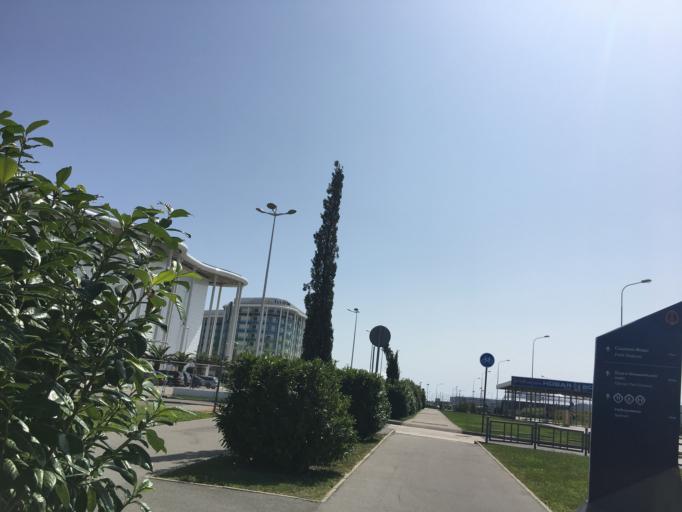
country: RU
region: Krasnodarskiy
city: Adler
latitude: 43.4138
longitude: 39.9484
